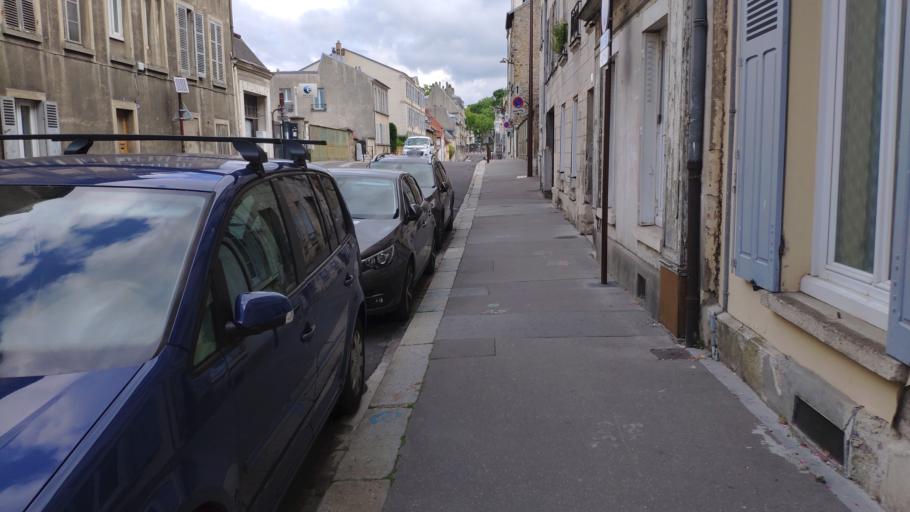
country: FR
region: Ile-de-France
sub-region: Departement des Yvelines
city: Versailles
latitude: 48.7976
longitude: 2.1376
